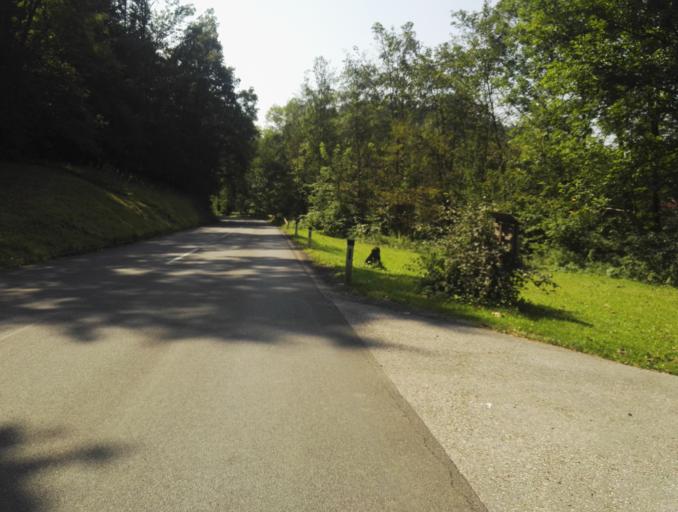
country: AT
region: Styria
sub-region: Politischer Bezirk Graz-Umgebung
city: Gratwein
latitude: 47.1239
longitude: 15.2986
